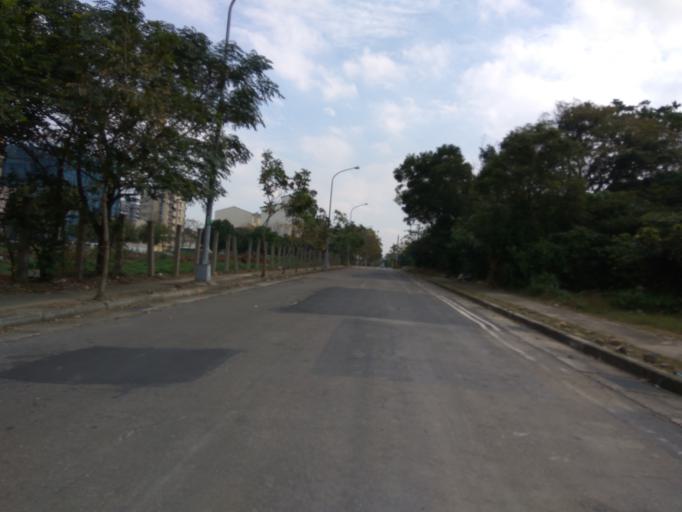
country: TW
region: Taiwan
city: Taoyuan City
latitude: 25.0038
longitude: 121.2188
